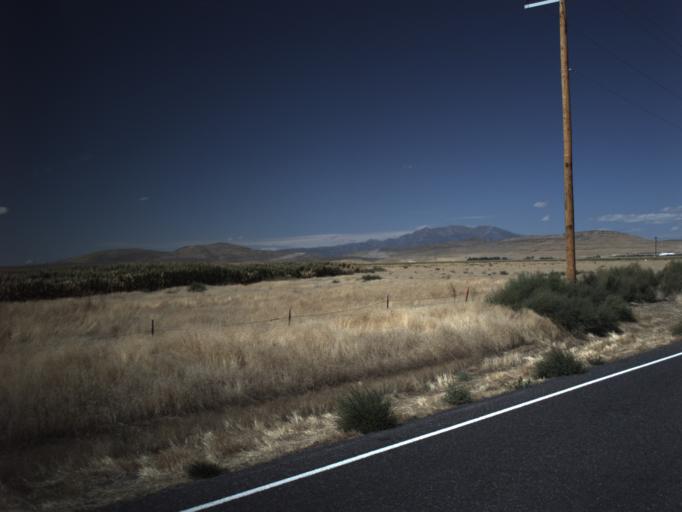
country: US
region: Utah
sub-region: Utah County
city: Genola
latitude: 40.0801
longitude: -111.9587
